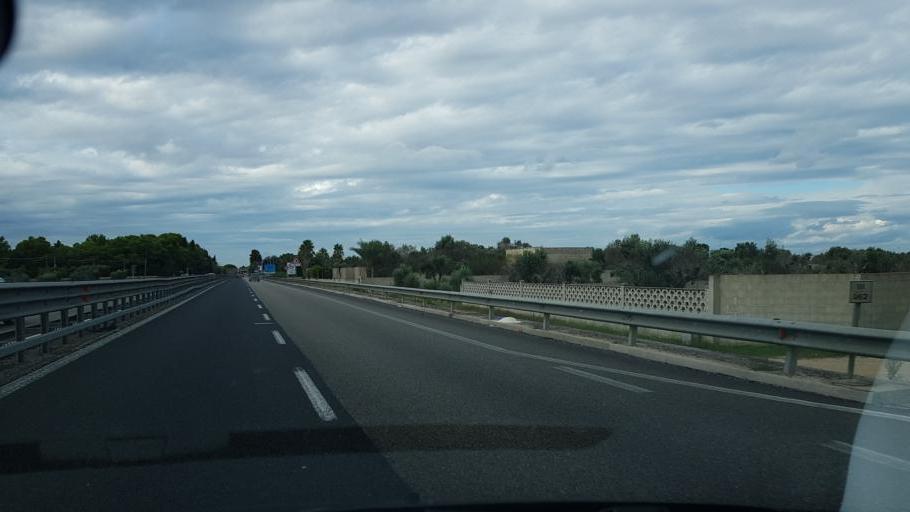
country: IT
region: Apulia
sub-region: Provincia di Lecce
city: Cavallino
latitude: 40.3013
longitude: 18.1931
